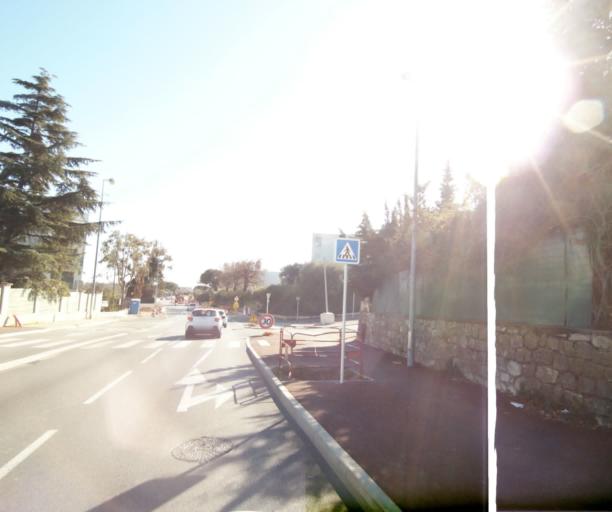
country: FR
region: Provence-Alpes-Cote d'Azur
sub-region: Departement des Alpes-Maritimes
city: Antibes
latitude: 43.5939
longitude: 7.1106
